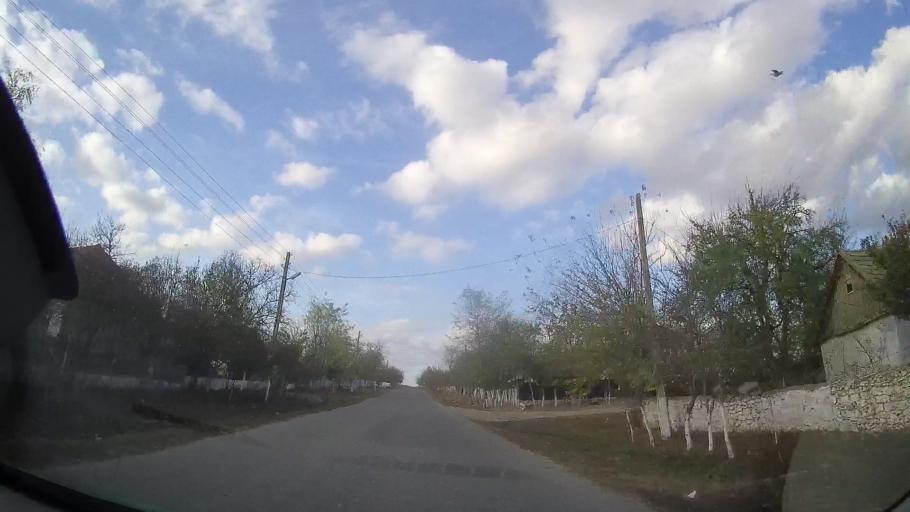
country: RO
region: Constanta
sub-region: Comuna Cerchezu
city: Cerchezu
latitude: 43.8615
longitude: 28.1011
